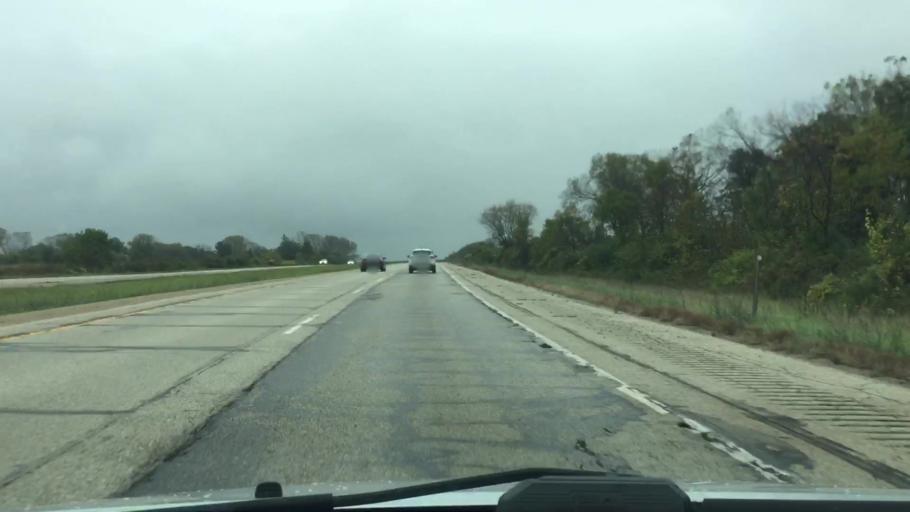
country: US
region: Wisconsin
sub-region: Walworth County
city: Como
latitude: 42.6328
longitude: -88.4751
